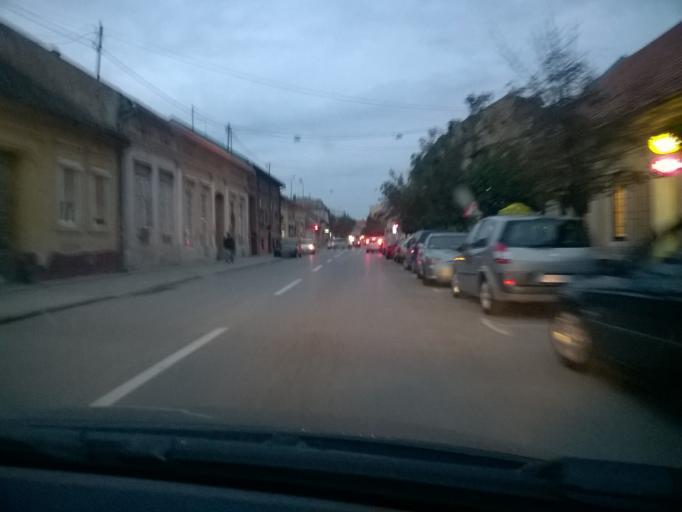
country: RS
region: Autonomna Pokrajina Vojvodina
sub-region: Juznobanatski Okrug
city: Pancevo
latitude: 44.8659
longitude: 20.6436
